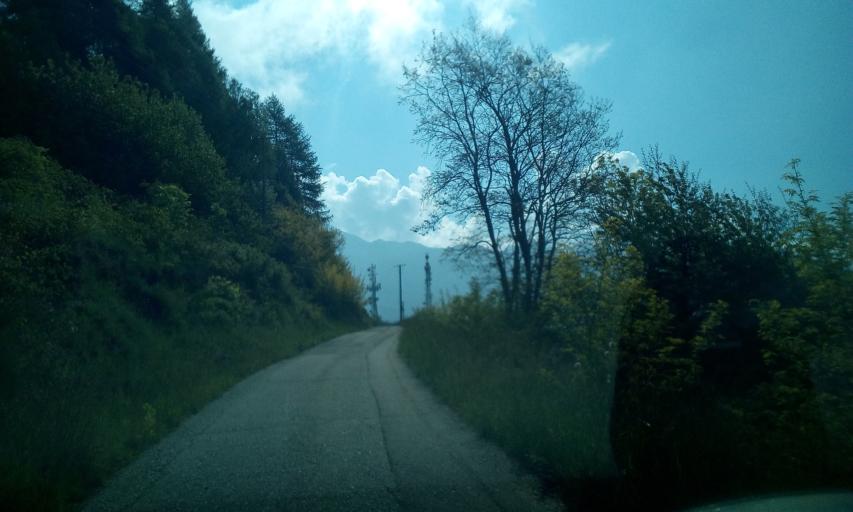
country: IT
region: Aosta Valley
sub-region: Valle d'Aosta
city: Torgnon
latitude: 45.8101
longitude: 7.5762
